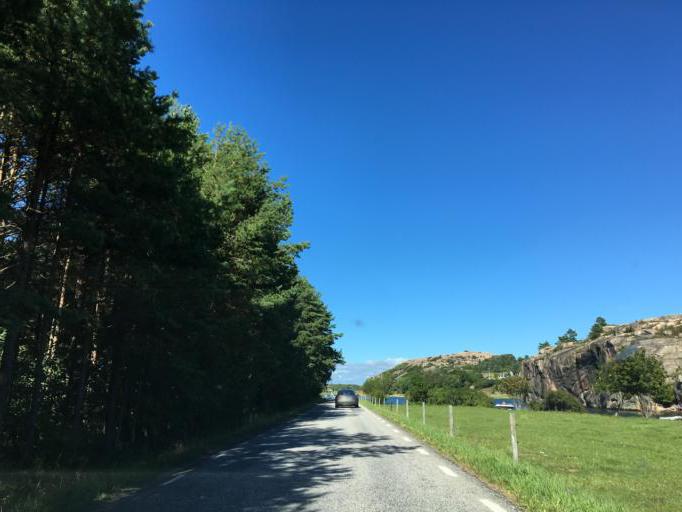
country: SE
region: Vaestra Goetaland
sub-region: Sotenas Kommun
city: Hunnebostrand
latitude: 58.4150
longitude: 11.2654
